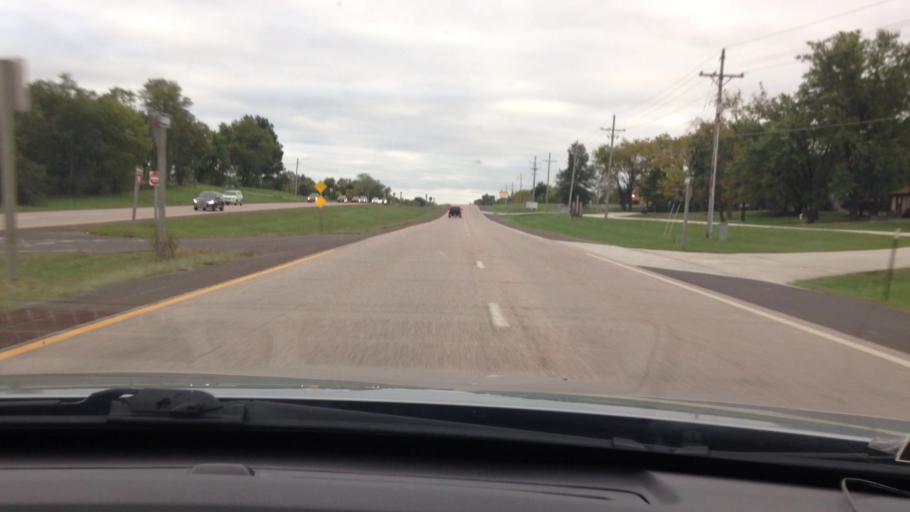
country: US
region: Kansas
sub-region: Leavenworth County
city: Lansing
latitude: 39.2076
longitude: -94.9004
